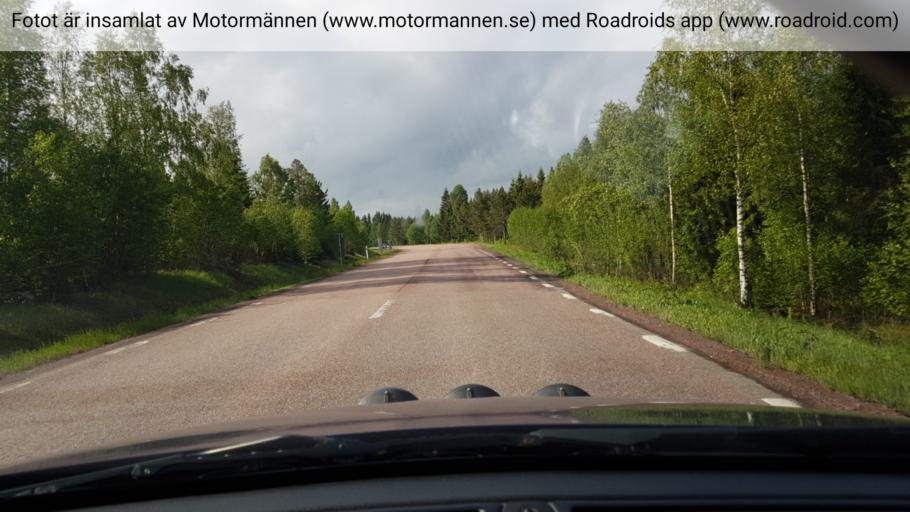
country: SE
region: Dalarna
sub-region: Orsa Kommun
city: Orsa
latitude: 61.0579
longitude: 14.6105
